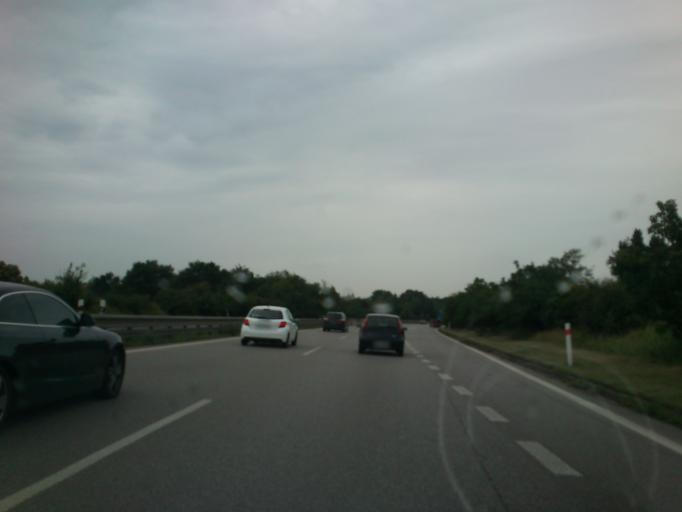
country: CZ
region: Central Bohemia
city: Brandys nad Labem-Stara Boleslav
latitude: 50.2009
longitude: 14.6914
